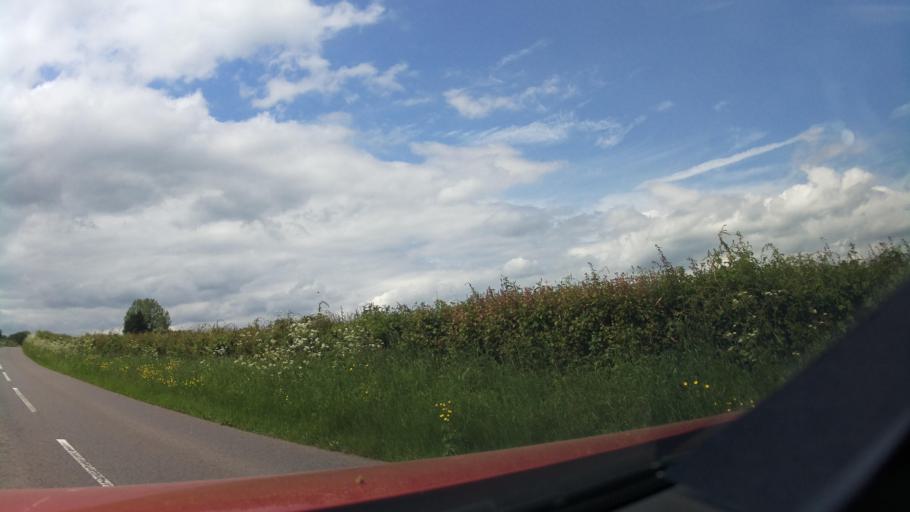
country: GB
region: England
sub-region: Herefordshire
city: Llanrothal
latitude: 51.8474
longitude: -2.7916
